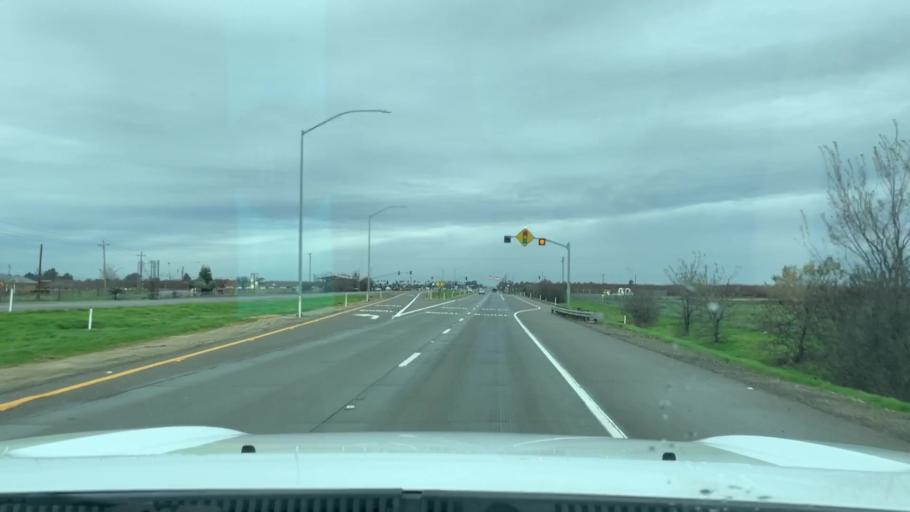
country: US
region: California
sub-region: Kings County
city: Lemoore
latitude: 36.3107
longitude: -119.8077
